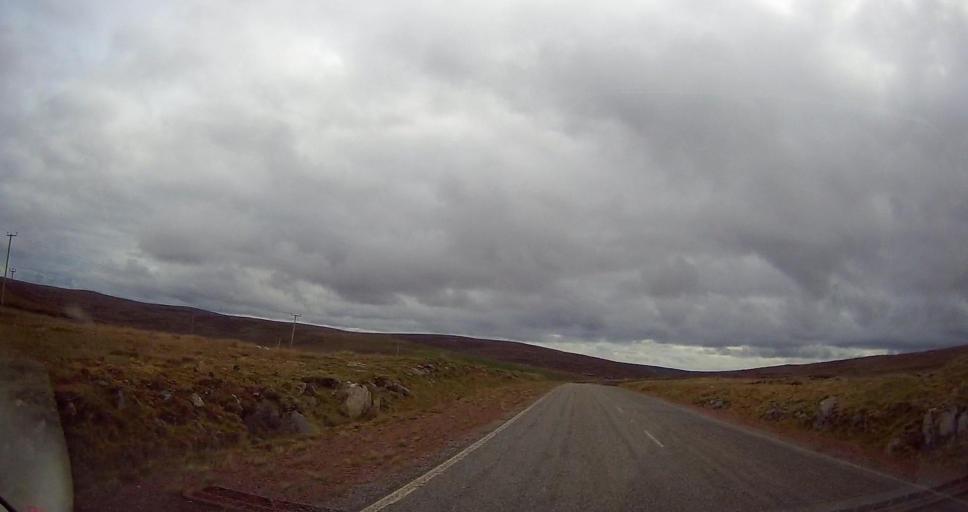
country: GB
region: Scotland
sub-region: Shetland Islands
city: Shetland
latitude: 60.6006
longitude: -1.1308
